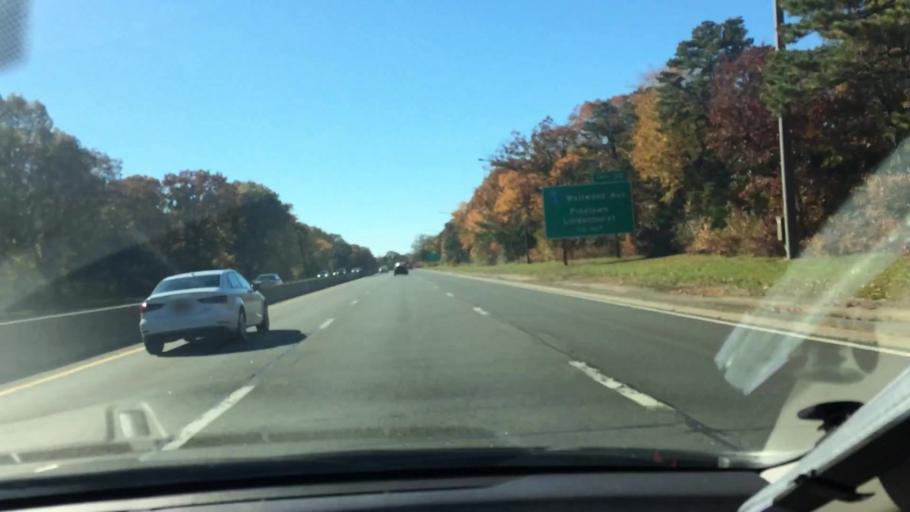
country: US
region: New York
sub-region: Suffolk County
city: North Lindenhurst
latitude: 40.7244
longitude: -73.3857
